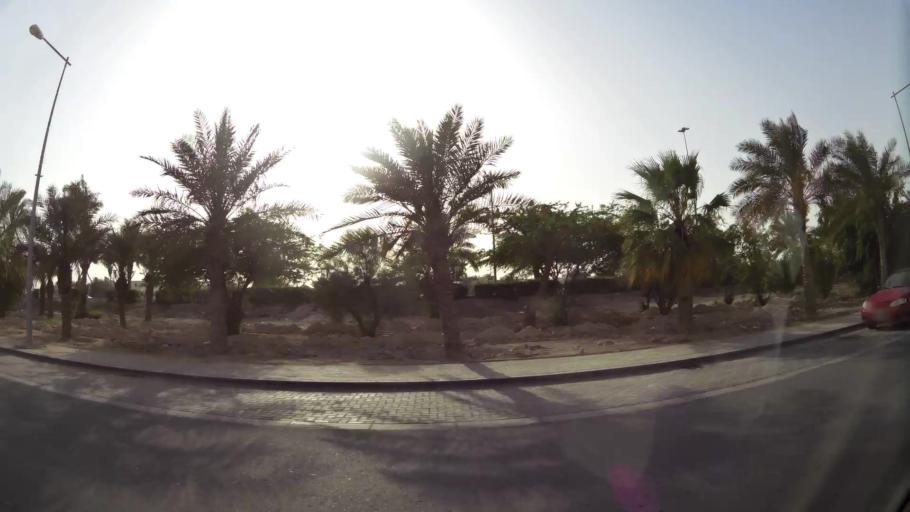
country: QA
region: Baladiyat ar Rayyan
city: Ar Rayyan
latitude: 25.2306
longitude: 51.4319
